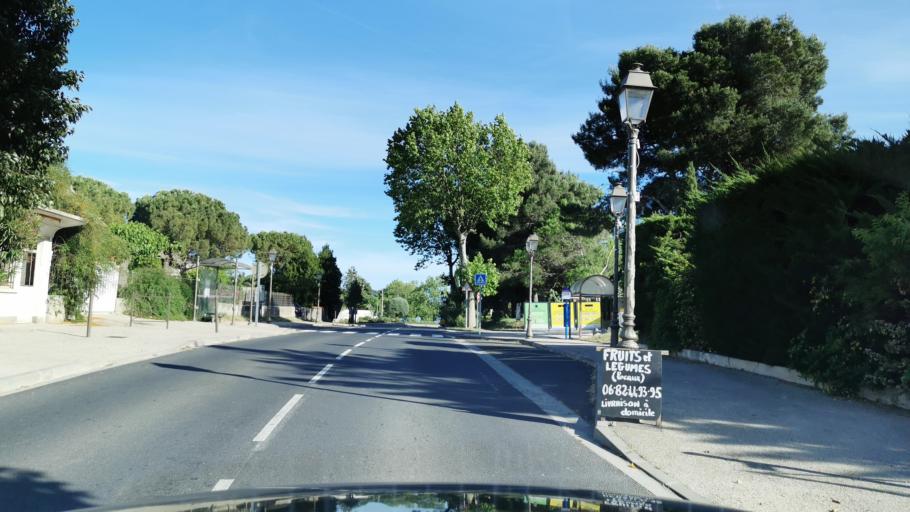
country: FR
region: Languedoc-Roussillon
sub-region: Departement de l'Aude
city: Marcorignan
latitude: 43.2236
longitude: 2.9233
